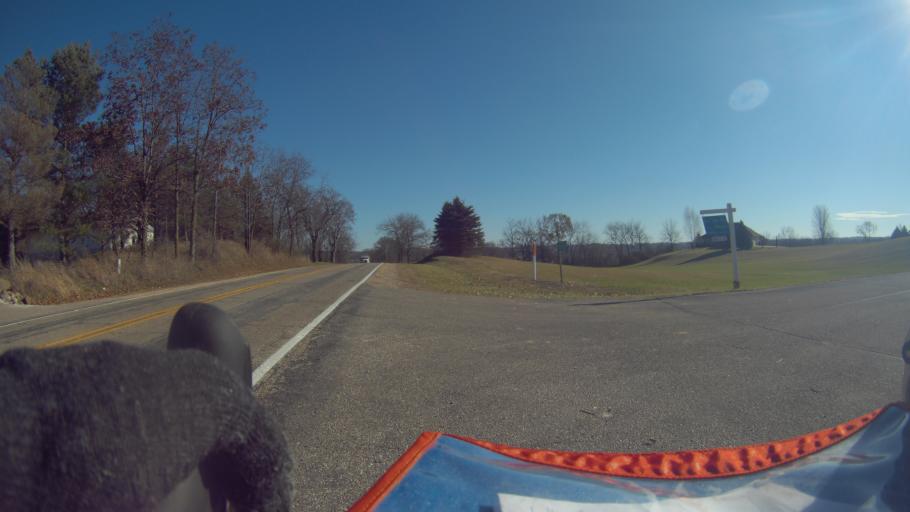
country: US
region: Wisconsin
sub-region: Dane County
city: Fitchburg
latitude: 42.8965
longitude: -89.4545
